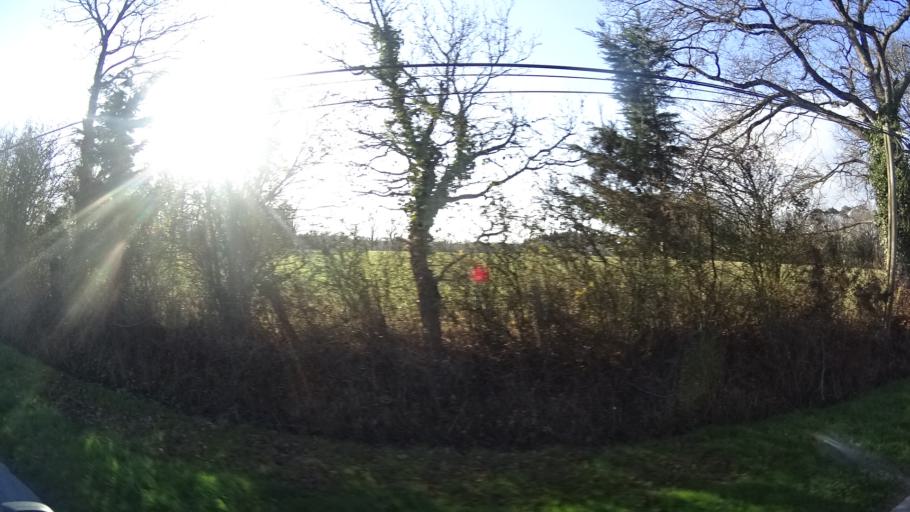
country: FR
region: Pays de la Loire
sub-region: Departement de la Loire-Atlantique
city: Plesse
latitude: 47.5331
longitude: -1.8869
